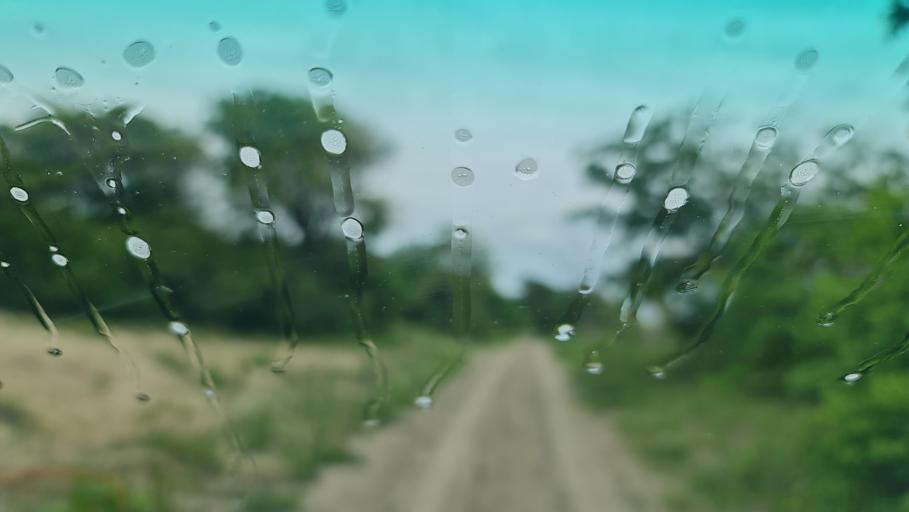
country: MZ
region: Maputo City
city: Maputo
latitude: -25.6977
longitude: 32.7060
